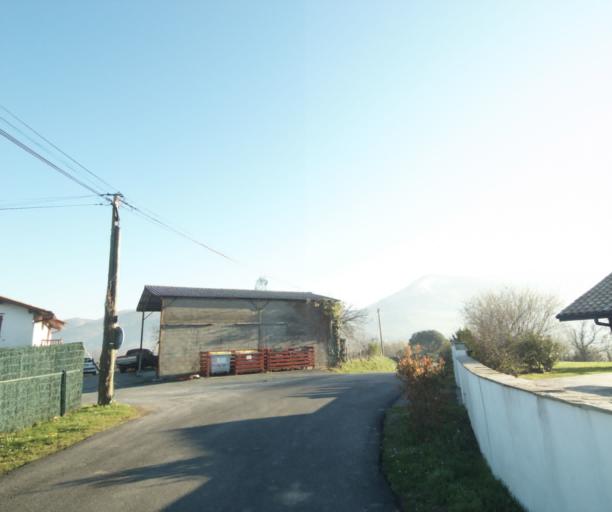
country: FR
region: Aquitaine
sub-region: Departement des Pyrenees-Atlantiques
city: Urrugne
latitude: 43.3447
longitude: -1.7013
